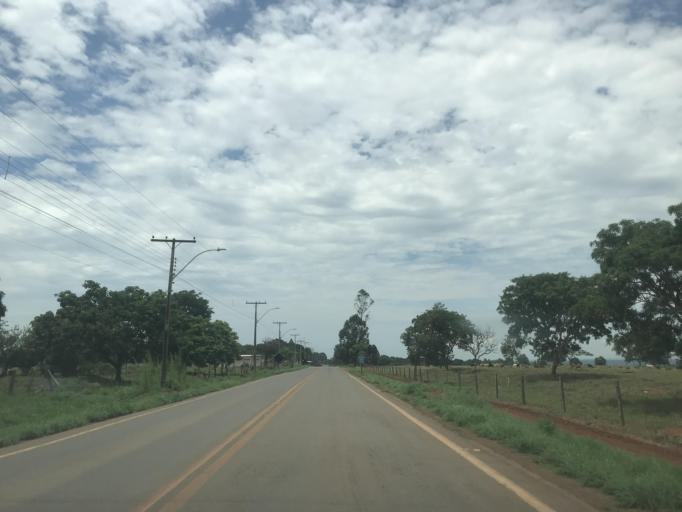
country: BR
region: Goias
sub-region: Luziania
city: Luziania
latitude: -16.3151
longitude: -48.0159
